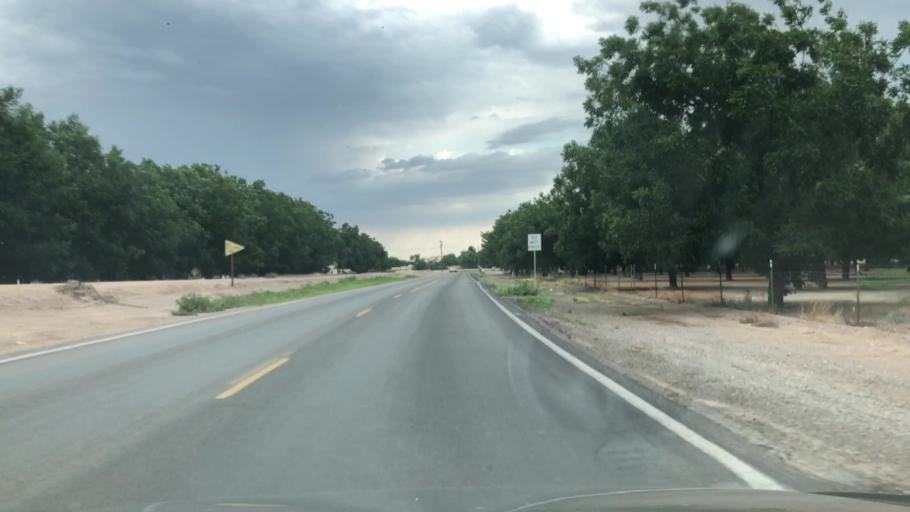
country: US
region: New Mexico
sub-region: Dona Ana County
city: La Union
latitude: 32.0046
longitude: -106.6606
